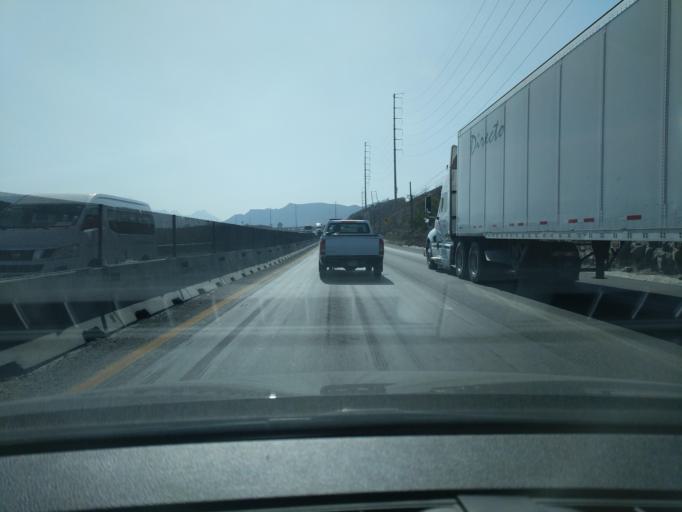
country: MX
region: Nuevo Leon
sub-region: Garcia
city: Los Parques
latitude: 25.7538
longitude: -100.5025
